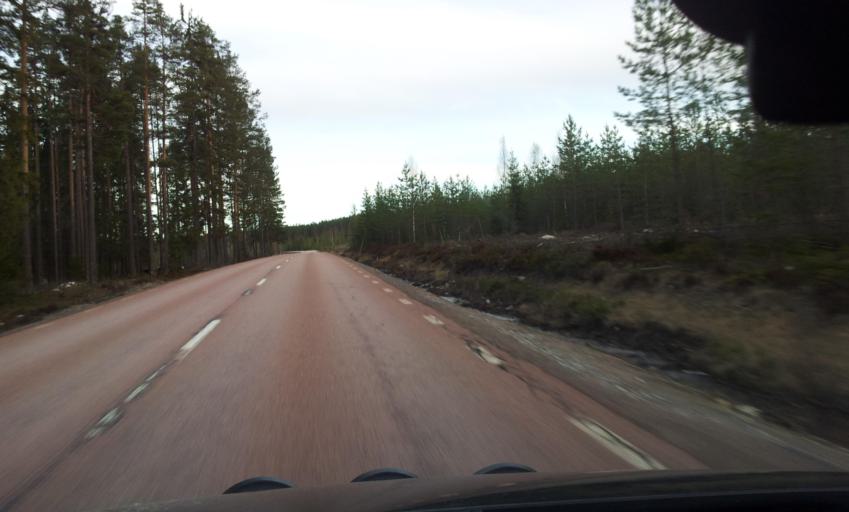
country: SE
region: Gaevleborg
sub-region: Ljusdals Kommun
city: Farila
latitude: 61.9763
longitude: 15.8599
